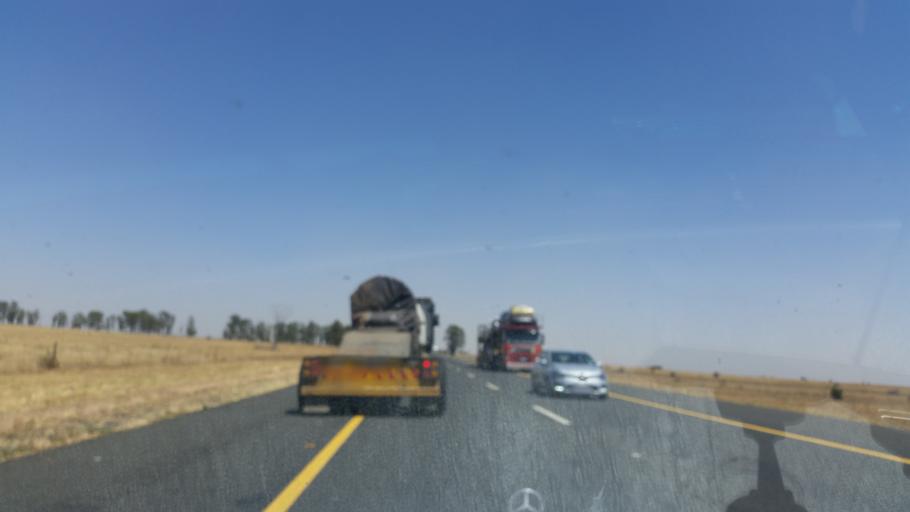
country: ZA
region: Orange Free State
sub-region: Lejweleputswa District Municipality
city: Winburg
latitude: -28.6390
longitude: 26.8928
